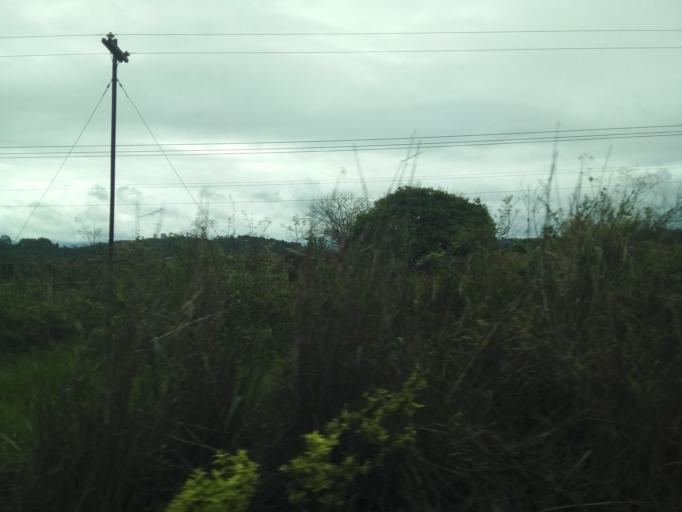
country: BR
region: Minas Gerais
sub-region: Ipatinga
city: Ipatinga
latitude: -19.4657
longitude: -42.4769
